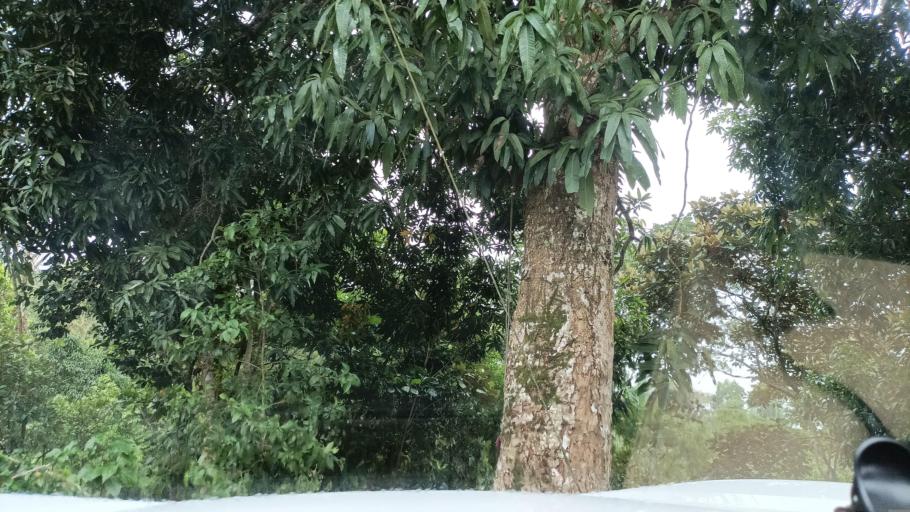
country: MX
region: Veracruz
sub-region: Moloacan
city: Cuichapa
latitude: 17.9206
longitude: -94.3674
